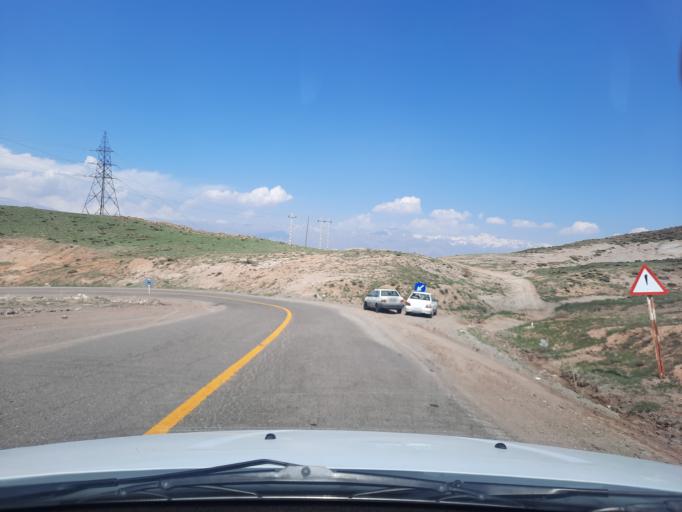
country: IR
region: Qazvin
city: Qazvin
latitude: 36.3942
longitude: 50.2111
